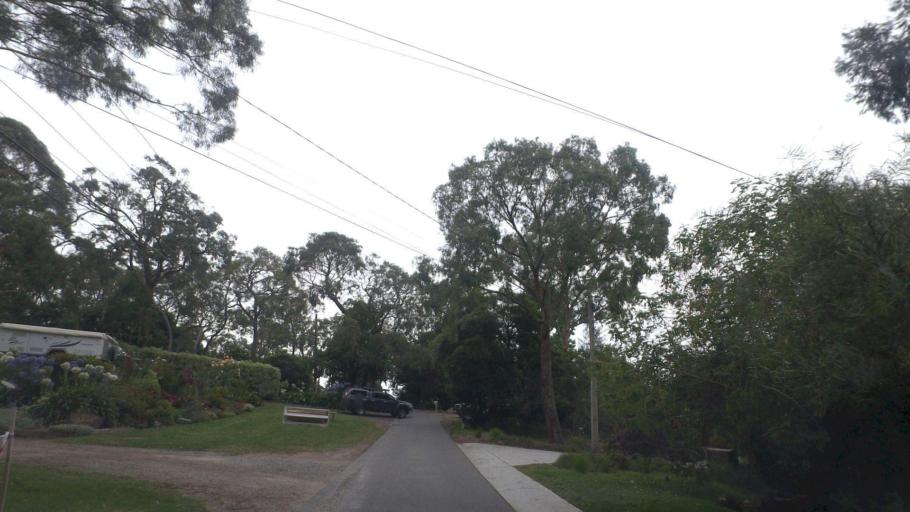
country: AU
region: Victoria
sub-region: Yarra Ranges
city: Kilsyth
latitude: -37.7907
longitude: 145.3366
